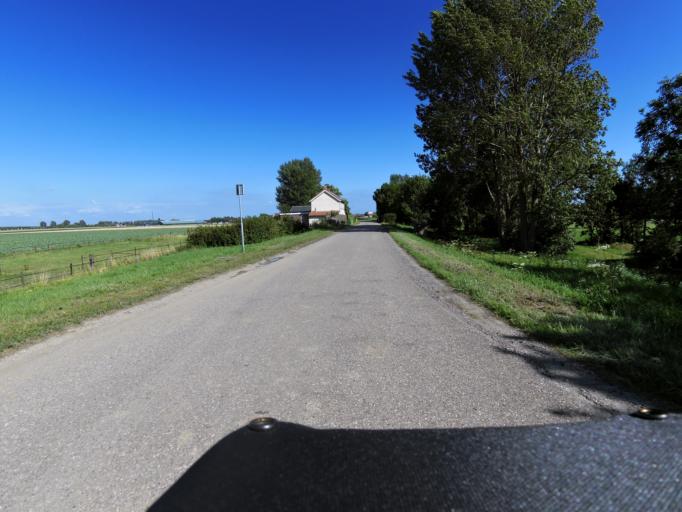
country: NL
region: South Holland
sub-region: Gemeente Goeree-Overflakkee
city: Dirksland
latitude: 51.7741
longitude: 4.0592
